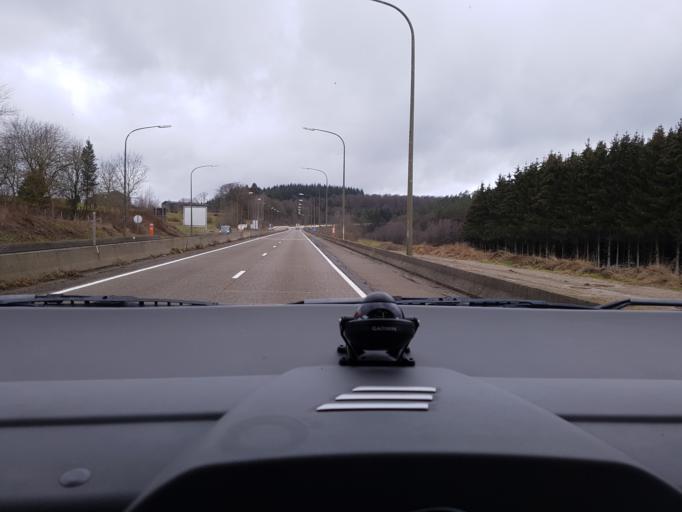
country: BE
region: Wallonia
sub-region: Province du Luxembourg
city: Tenneville
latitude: 50.0930
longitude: 5.4959
